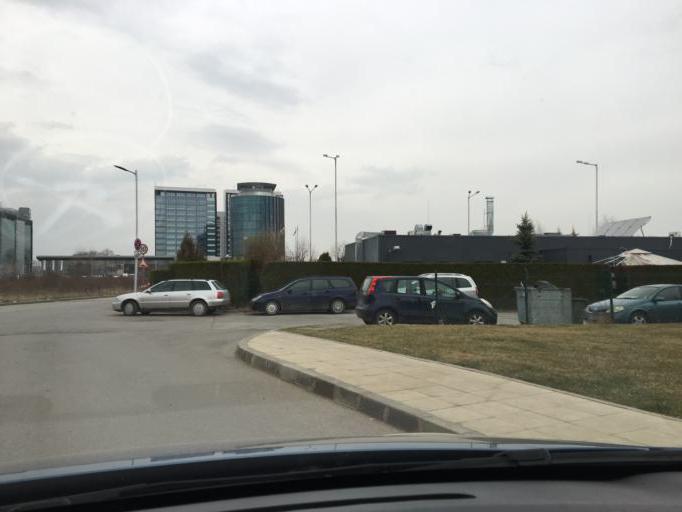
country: BG
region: Sofia-Capital
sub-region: Stolichna Obshtina
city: Sofia
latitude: 42.6800
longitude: 23.4035
